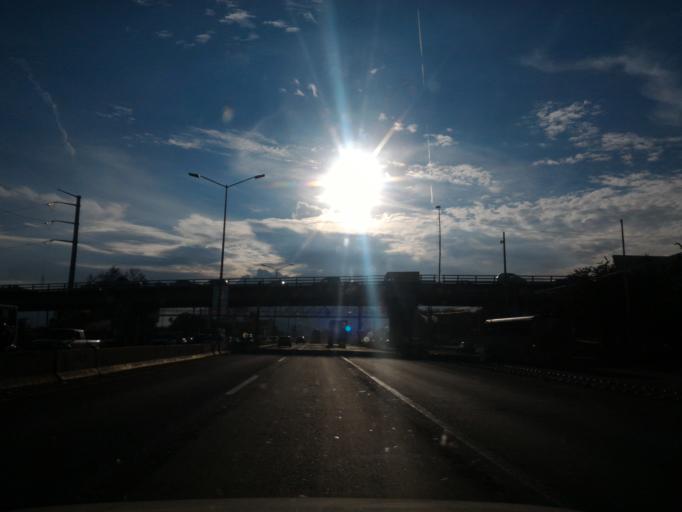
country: MX
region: Jalisco
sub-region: Tlajomulco de Zuniga
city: Altus Bosques
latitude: 20.5776
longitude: -103.3619
